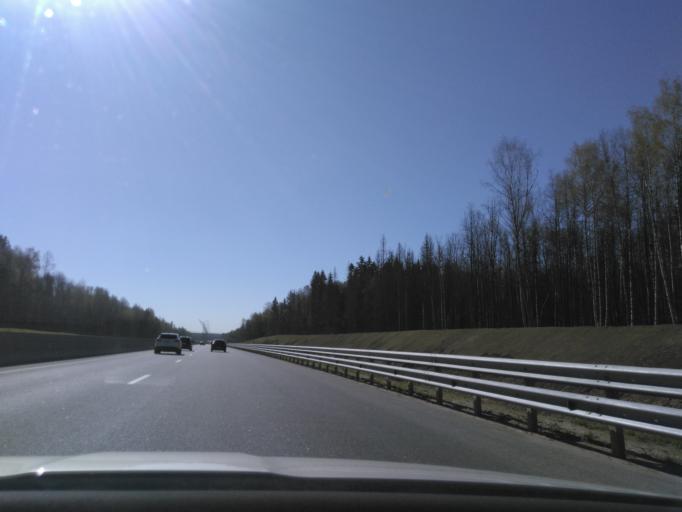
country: RU
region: Moskovskaya
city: Mendeleyevo
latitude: 56.0694
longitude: 37.2226
